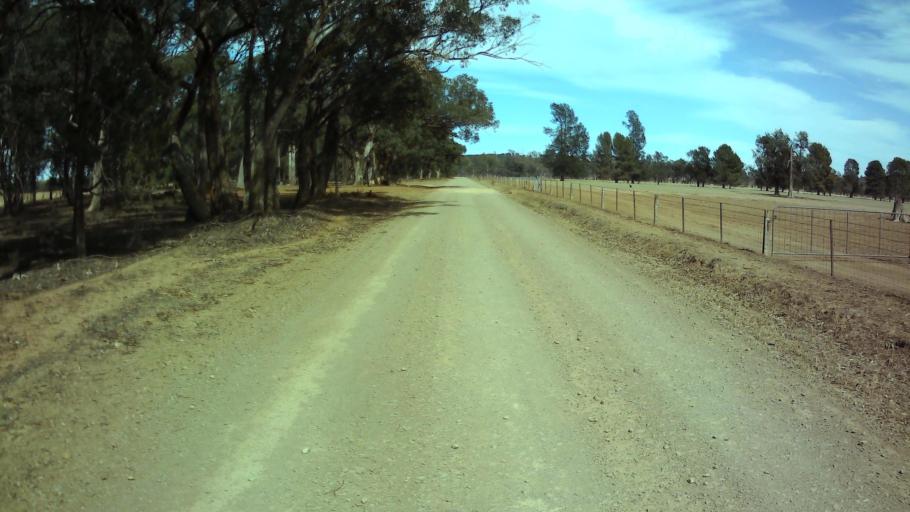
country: AU
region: New South Wales
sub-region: Weddin
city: Grenfell
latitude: -33.6849
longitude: 148.2898
